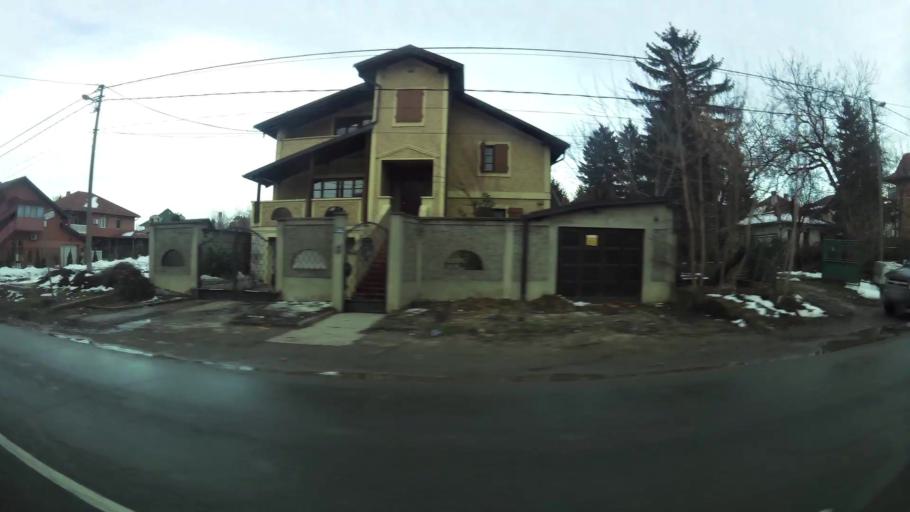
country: RS
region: Central Serbia
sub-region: Belgrade
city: Vozdovac
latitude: 44.7469
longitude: 20.4771
